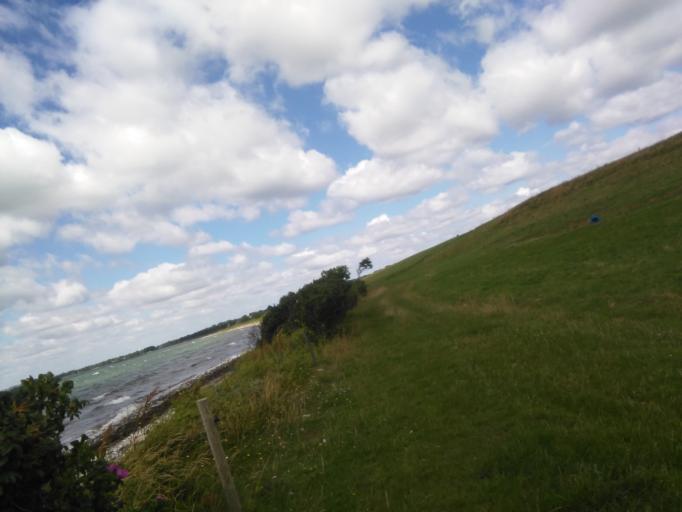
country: DK
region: Central Jutland
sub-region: Arhus Kommune
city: Logten
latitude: 56.1700
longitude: 10.3783
